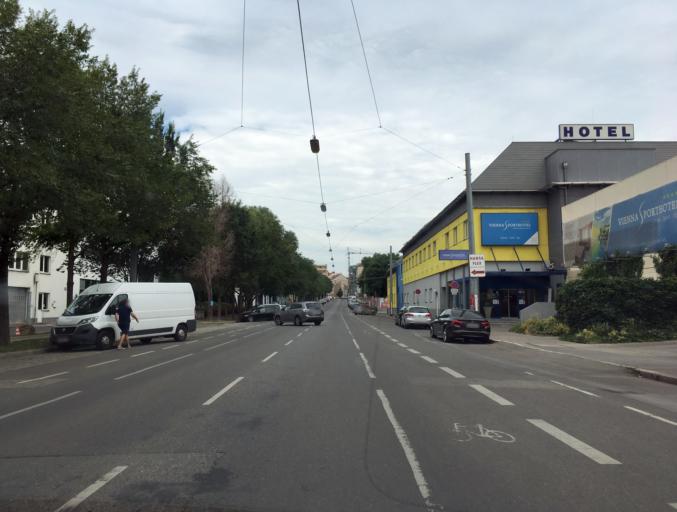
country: AT
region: Vienna
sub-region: Wien Stadt
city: Vienna
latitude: 48.1908
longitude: 16.4091
